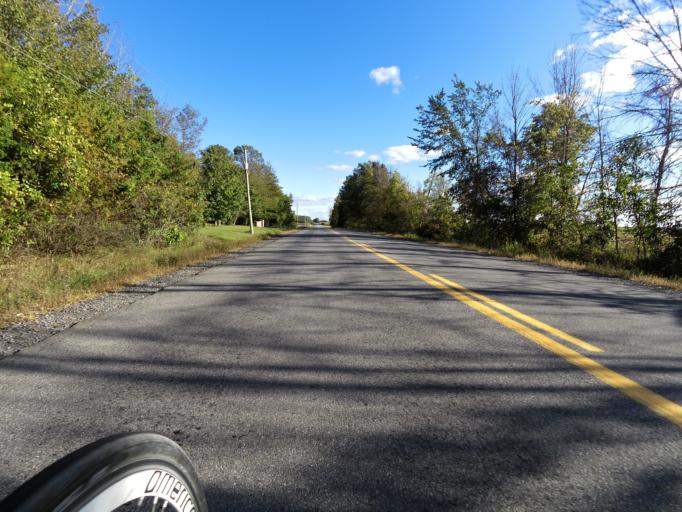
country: CA
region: Ontario
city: Bells Corners
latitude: 45.1397
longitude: -75.7603
